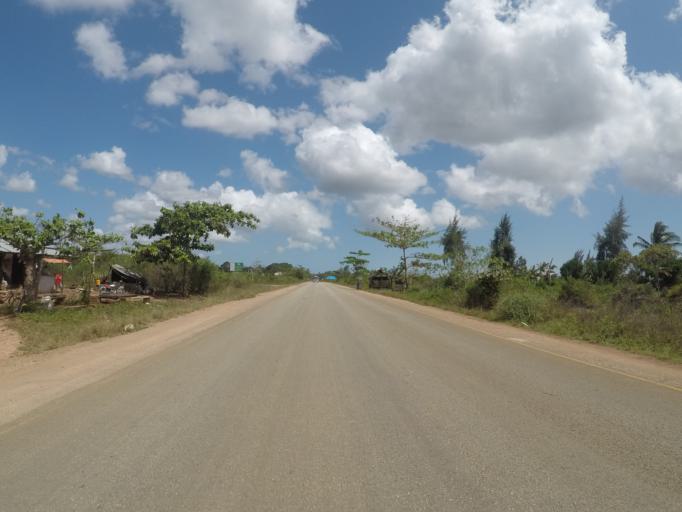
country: TZ
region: Zanzibar Central/South
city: Koani
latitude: -6.1583
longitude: 39.3298
